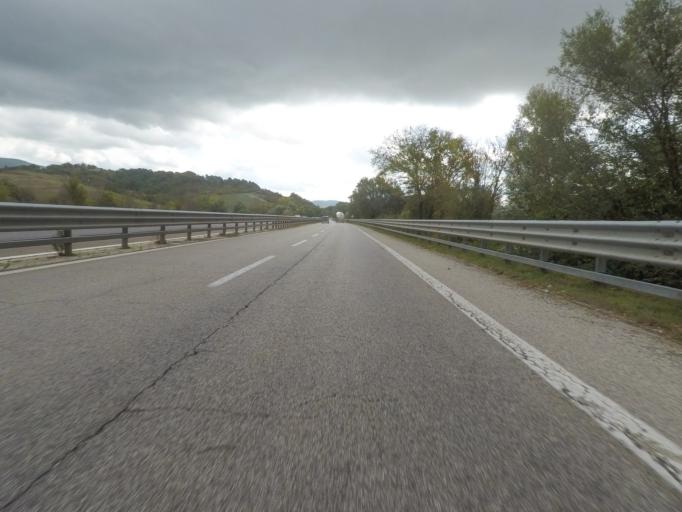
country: IT
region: Tuscany
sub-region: Provincia di Siena
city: Rapolano Terme
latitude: 43.3160
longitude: 11.5748
